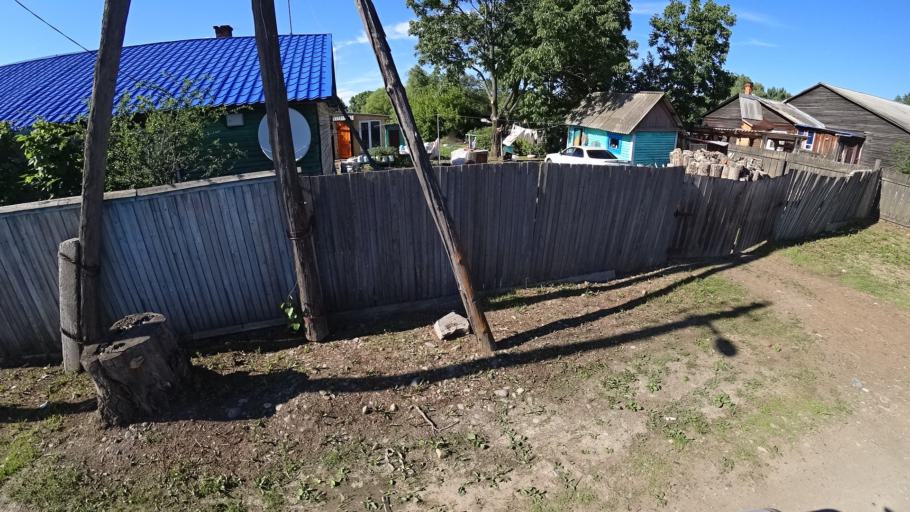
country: RU
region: Khabarovsk Krai
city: Khor
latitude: 47.8891
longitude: 134.9969
